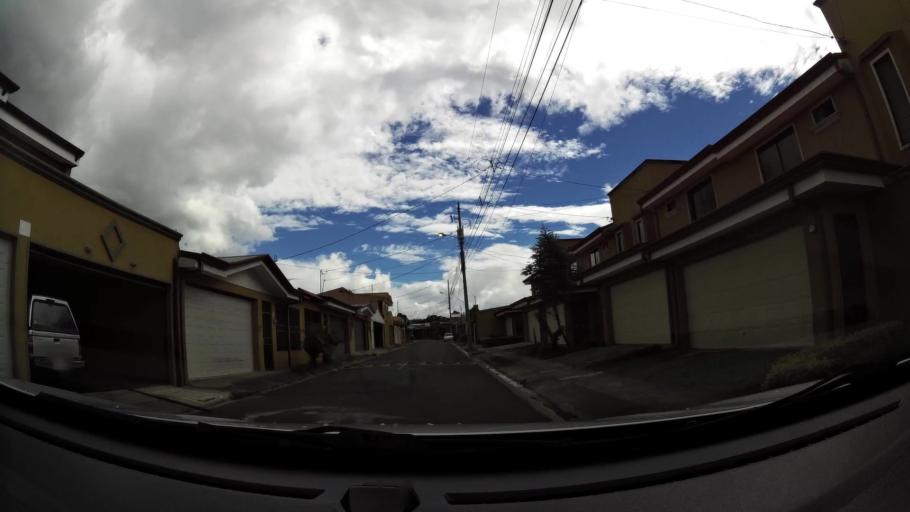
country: CR
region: Cartago
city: Concepcion
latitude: 9.9249
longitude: -84.0010
